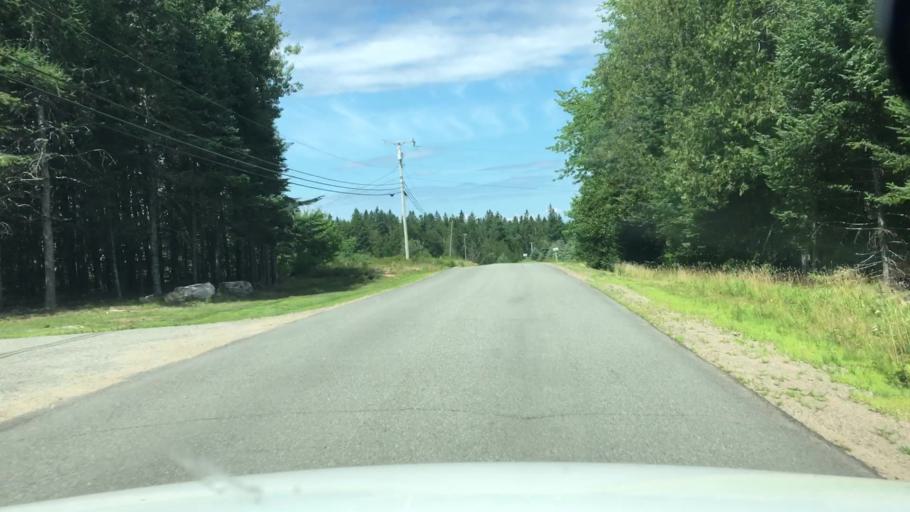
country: CA
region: New Brunswick
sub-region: Charlotte County
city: Saint Andrews
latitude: 44.9854
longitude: -67.0689
